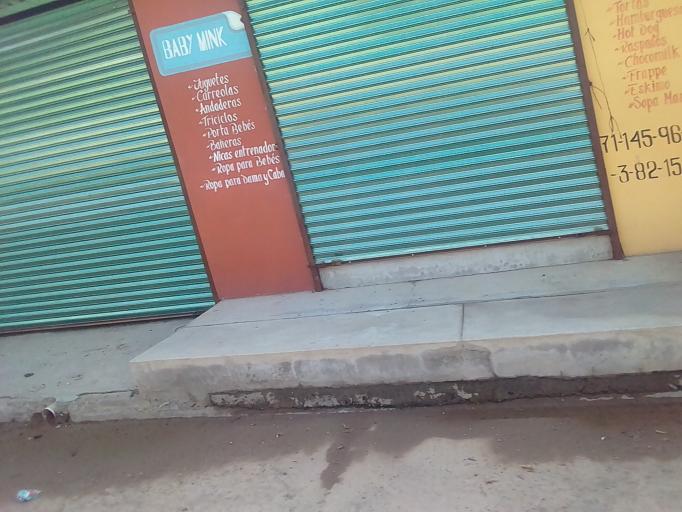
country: MX
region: Oaxaca
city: Union Hidalgo
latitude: 16.4723
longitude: -94.8355
